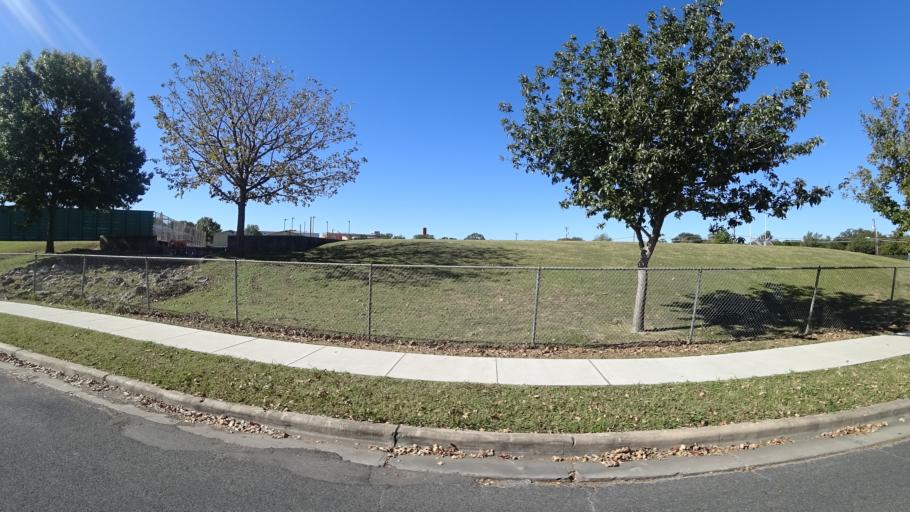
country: US
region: Texas
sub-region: Travis County
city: Rollingwood
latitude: 30.2870
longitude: -97.7727
